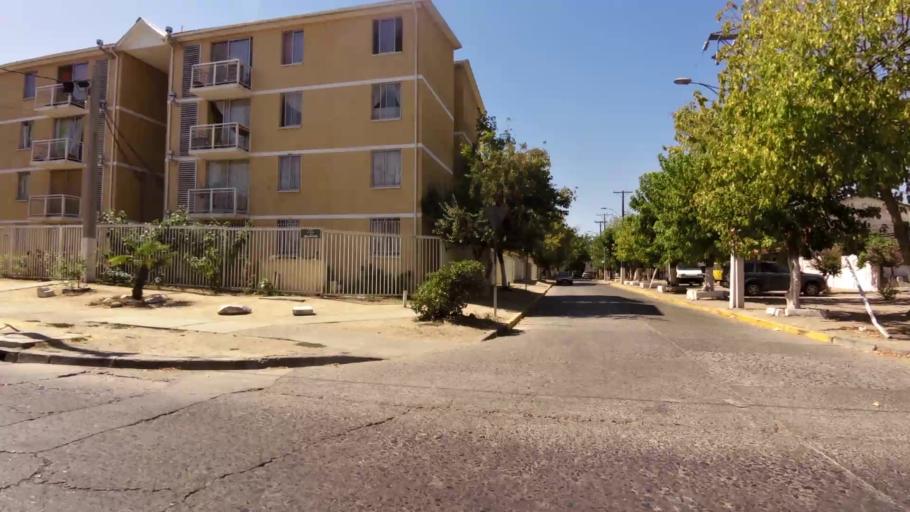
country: CL
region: Maule
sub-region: Provincia de Talca
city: Talca
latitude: -35.4150
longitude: -71.6503
